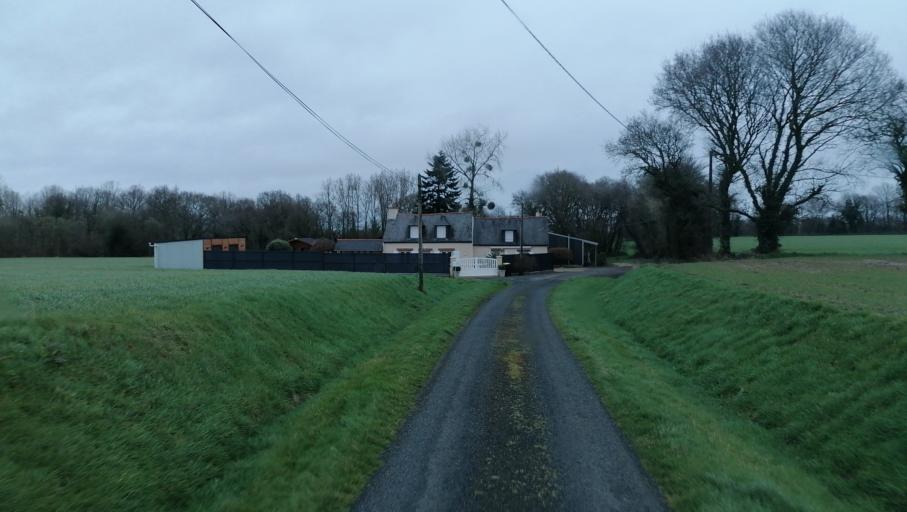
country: FR
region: Brittany
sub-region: Departement des Cotes-d'Armor
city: Lanrodec
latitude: 48.5629
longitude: -3.0489
